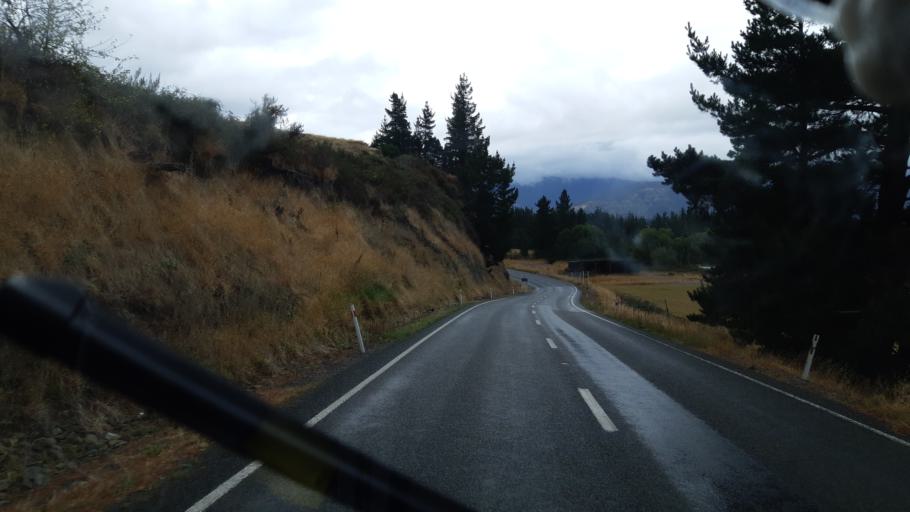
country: NZ
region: Canterbury
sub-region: Hurunui District
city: Amberley
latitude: -42.5819
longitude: 172.7742
